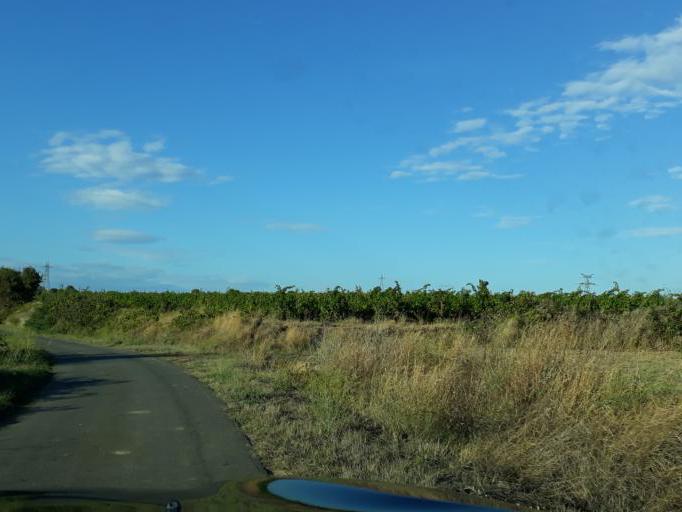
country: FR
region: Languedoc-Roussillon
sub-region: Departement de l'Herault
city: Florensac
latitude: 43.4083
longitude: 3.4761
